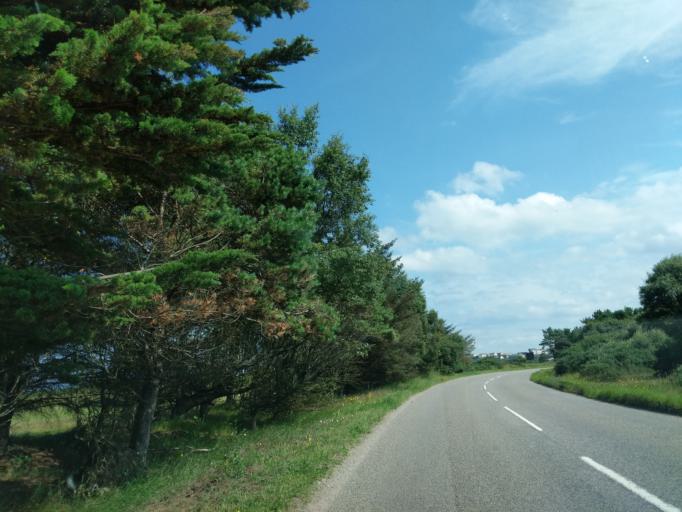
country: GB
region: Scotland
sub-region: Moray
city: Lossiemouth
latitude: 57.7188
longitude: -3.3214
